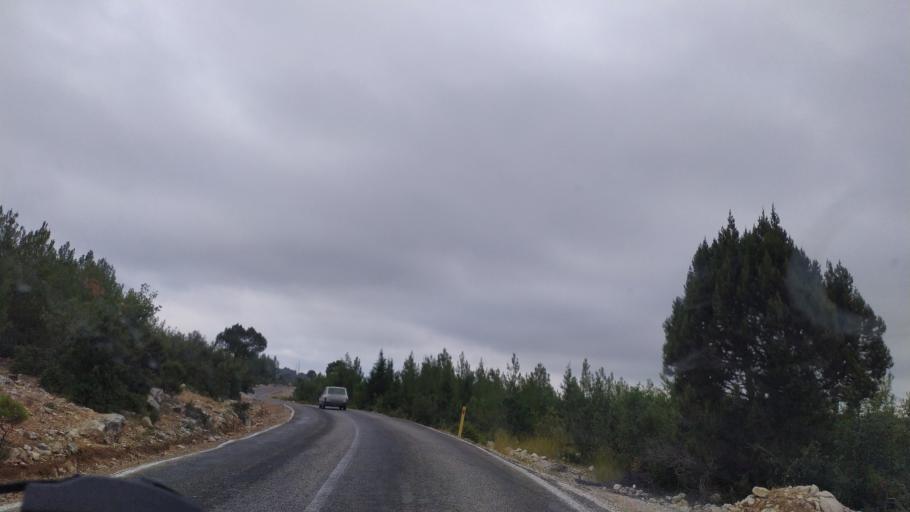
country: TR
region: Mersin
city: Silifke
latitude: 36.5432
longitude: 33.9275
